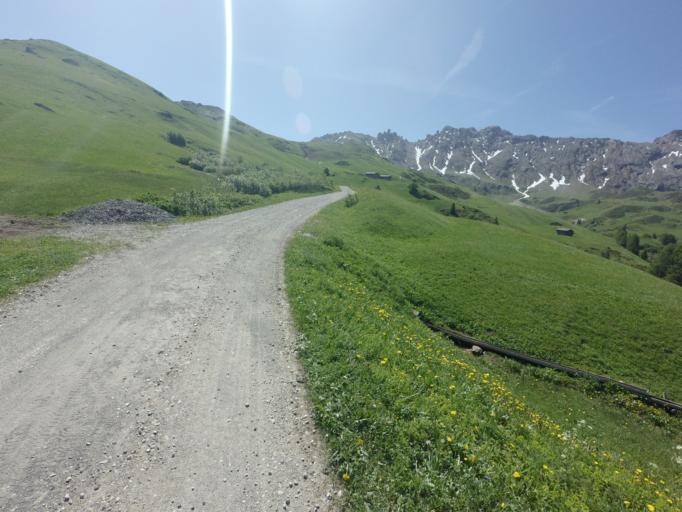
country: IT
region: Trentino-Alto Adige
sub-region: Bolzano
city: Ortisei
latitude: 46.5174
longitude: 11.6281
